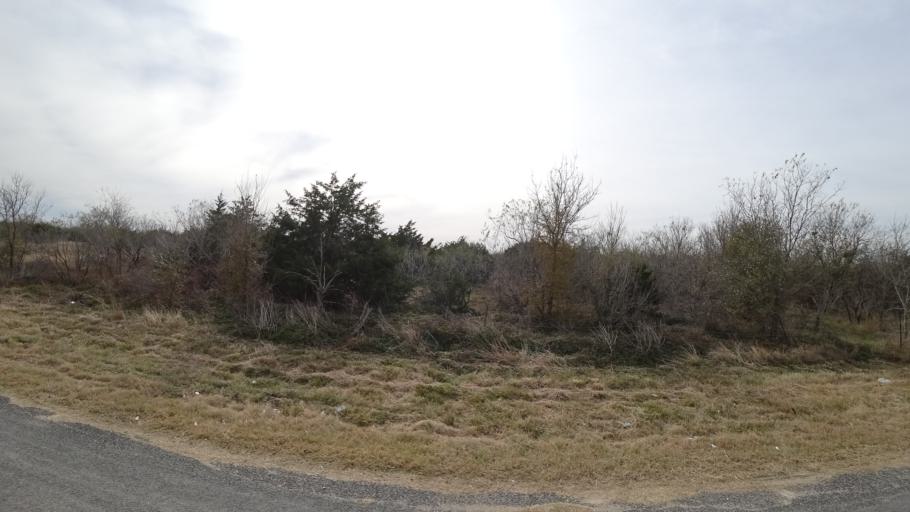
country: US
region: Texas
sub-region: Travis County
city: Garfield
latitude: 30.1232
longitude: -97.6152
